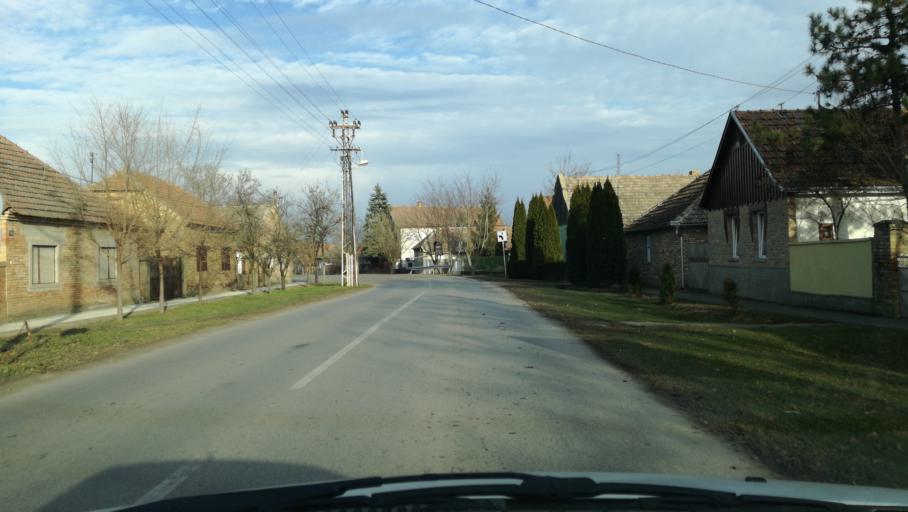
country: RS
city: Rusko Selo
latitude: 45.7629
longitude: 20.5849
